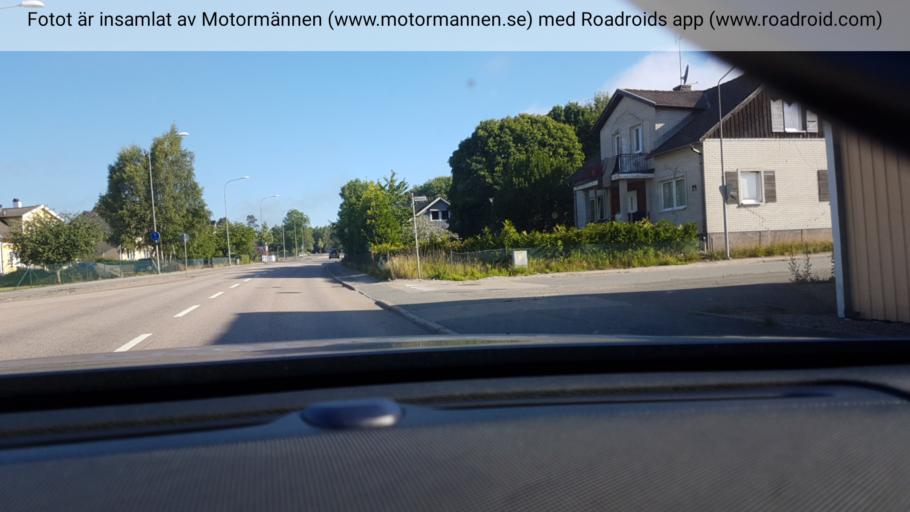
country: SE
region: Skane
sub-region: Hassleholms Kommun
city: Bjarnum
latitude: 56.2938
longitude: 13.7087
